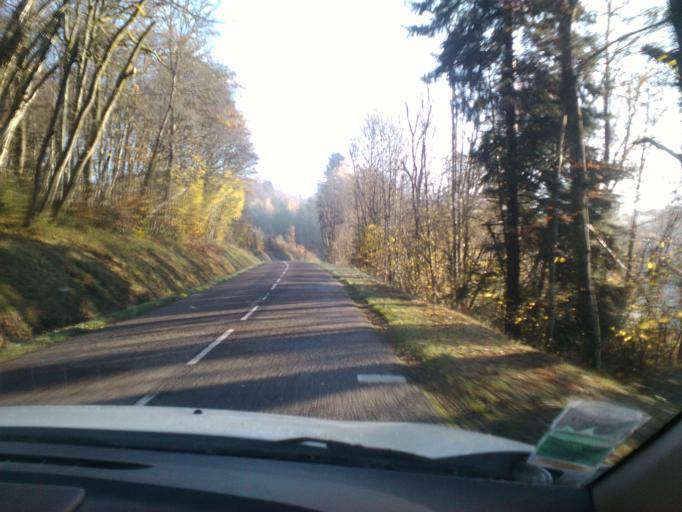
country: FR
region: Lorraine
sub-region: Departement des Vosges
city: Uzemain
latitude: 48.0581
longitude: 6.3468
